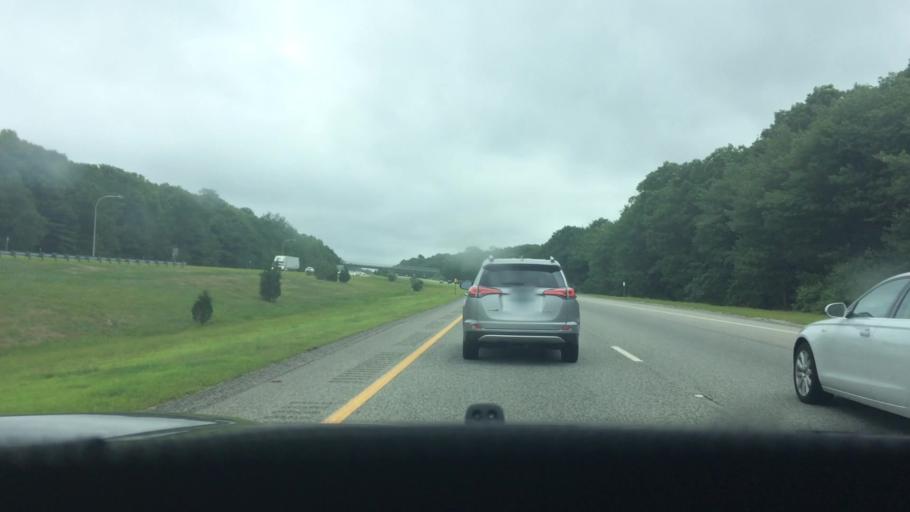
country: US
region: Rhode Island
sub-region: Kent County
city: West Greenwich
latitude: 41.5989
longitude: -71.6594
